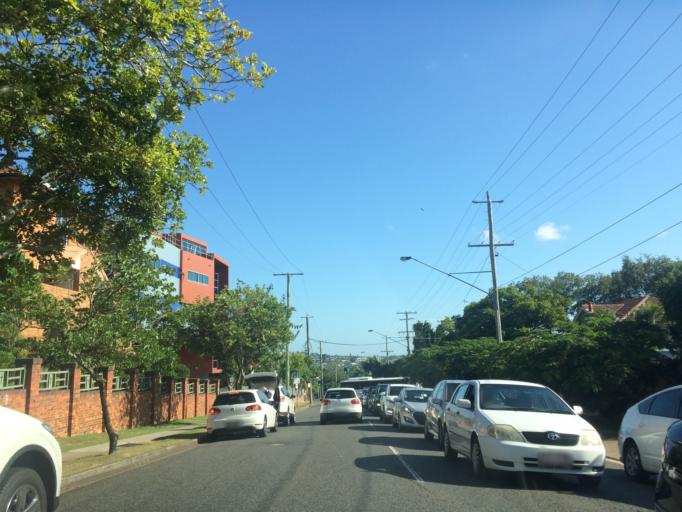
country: AU
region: Queensland
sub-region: Brisbane
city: Balmoral
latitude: -27.4704
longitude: 153.0590
